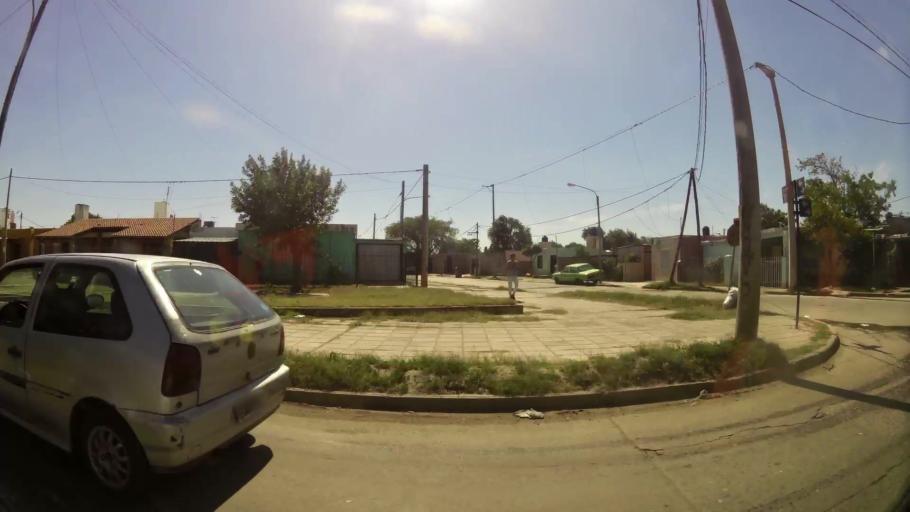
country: AR
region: Cordoba
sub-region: Departamento de Capital
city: Cordoba
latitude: -31.3714
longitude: -64.1555
